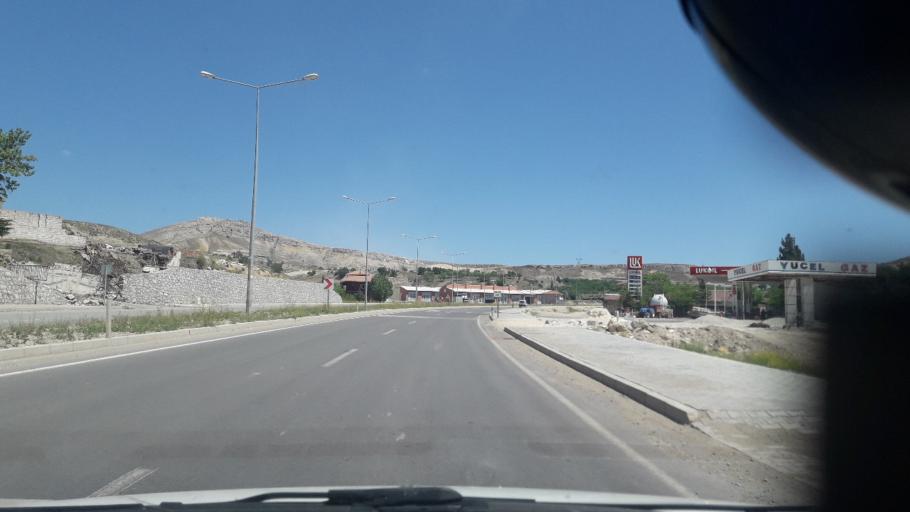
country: TR
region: Malatya
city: Hekimhan
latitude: 38.8182
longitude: 37.9420
